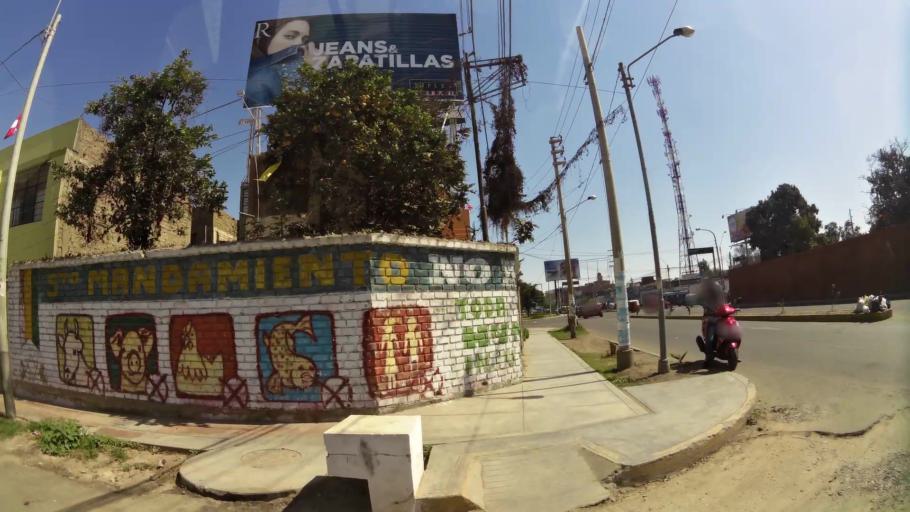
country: PE
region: Ica
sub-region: Provincia de Ica
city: Ica
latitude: -14.0711
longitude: -75.7319
